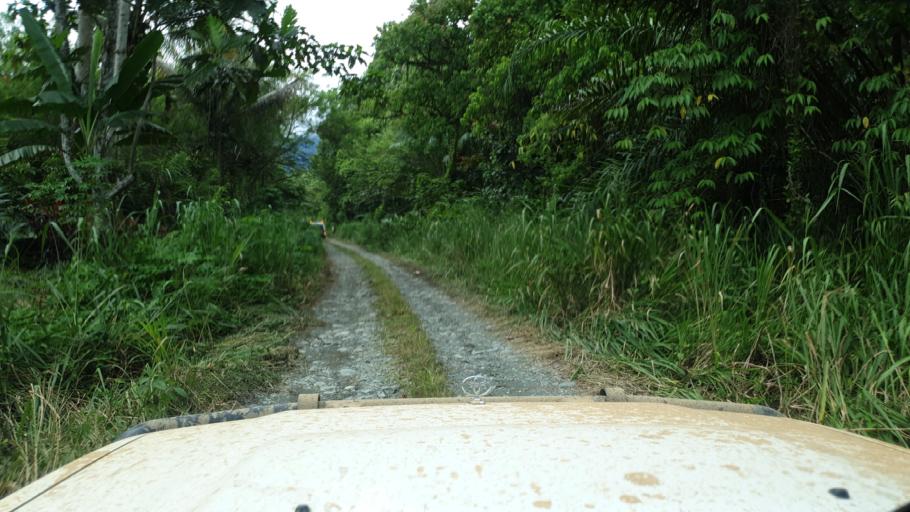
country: PG
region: Northern Province
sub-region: Sohe
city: Kokoda
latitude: -8.9279
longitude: 147.8692
